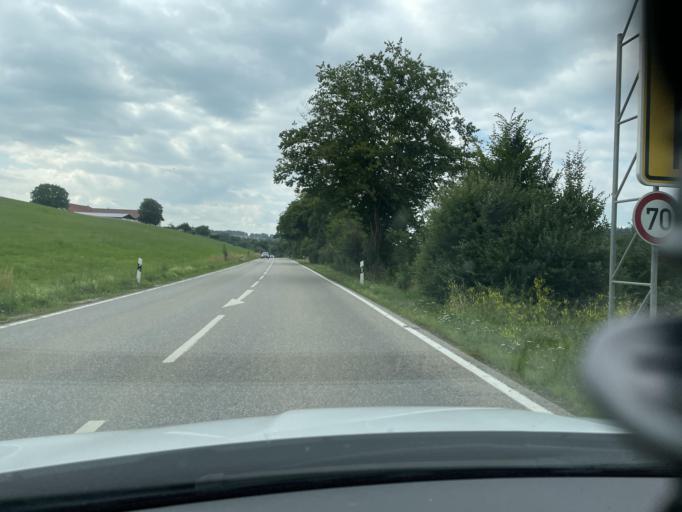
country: DE
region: Bavaria
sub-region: Upper Bavaria
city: Sankt Wolfgang
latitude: 48.2032
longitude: 12.1445
